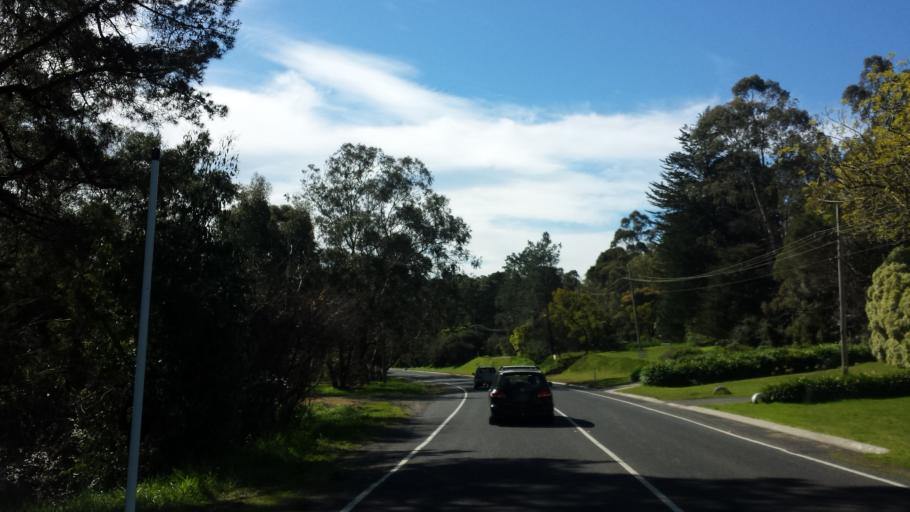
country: AU
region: Victoria
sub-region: Maroondah
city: Warranwood
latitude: -37.7832
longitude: 145.2335
